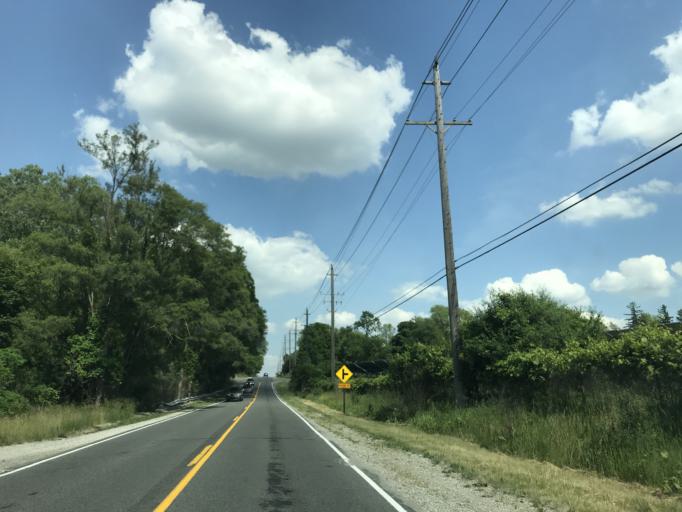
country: US
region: Michigan
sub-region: Washtenaw County
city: Ypsilanti
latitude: 42.2607
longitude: -83.6097
